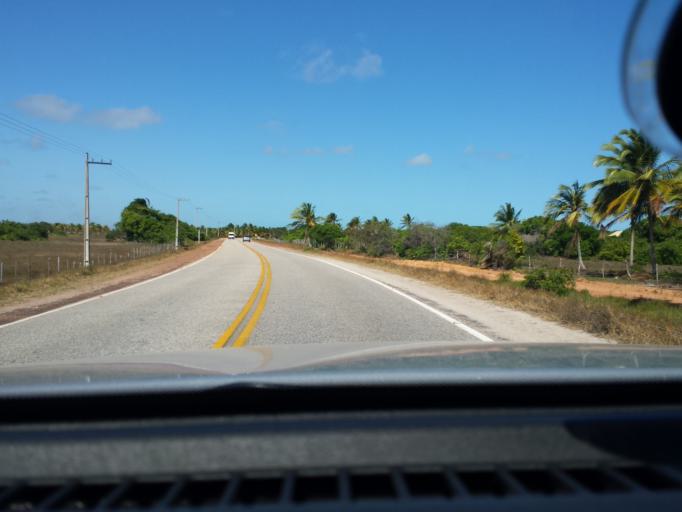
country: BR
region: Sergipe
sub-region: Estancia
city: Estancia
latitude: -11.2653
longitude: -37.2650
